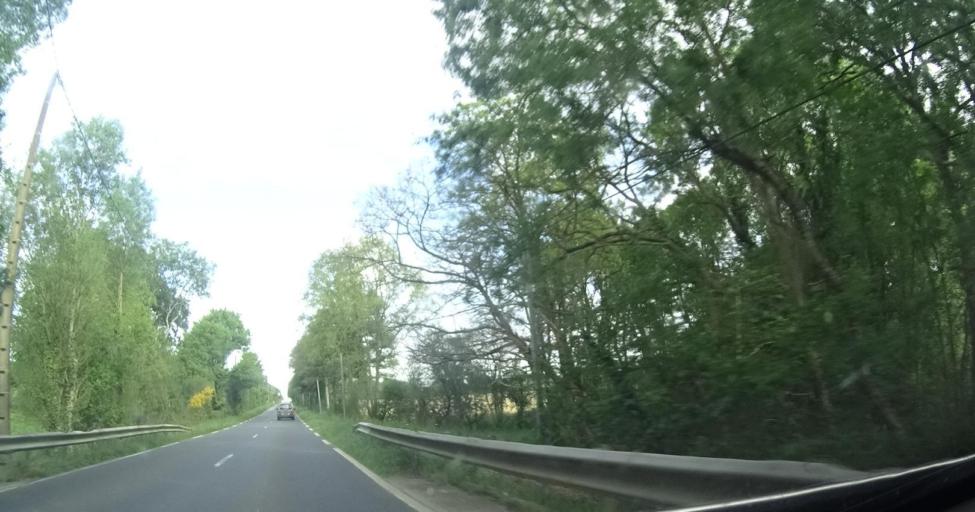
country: FR
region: Pays de la Loire
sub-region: Departement de la Loire-Atlantique
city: Fay-de-Bretagne
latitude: 47.4115
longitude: -1.7669
